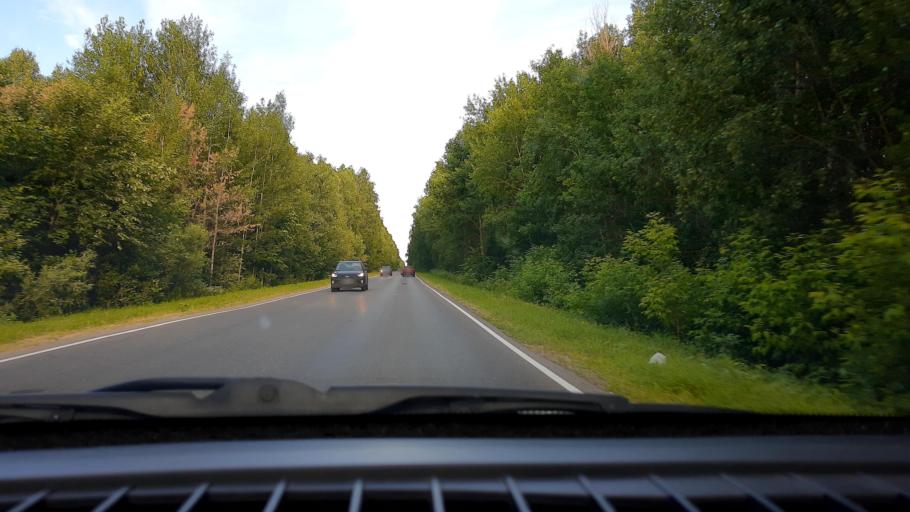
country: RU
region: Nizjnij Novgorod
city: Afonino
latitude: 56.3074
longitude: 44.2421
